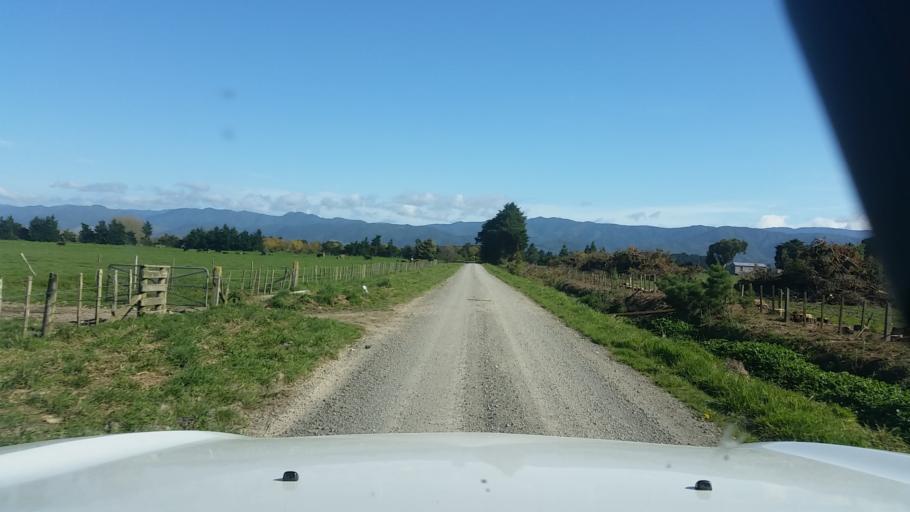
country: NZ
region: Wellington
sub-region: South Wairarapa District
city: Waipawa
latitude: -41.1444
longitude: 175.3982
